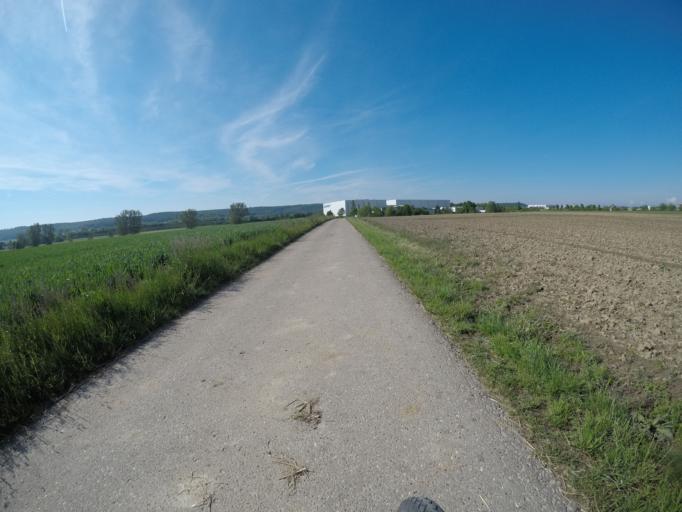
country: DE
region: Baden-Wuerttemberg
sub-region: Regierungsbezirk Stuttgart
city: Gartringen
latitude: 48.6426
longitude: 8.9208
